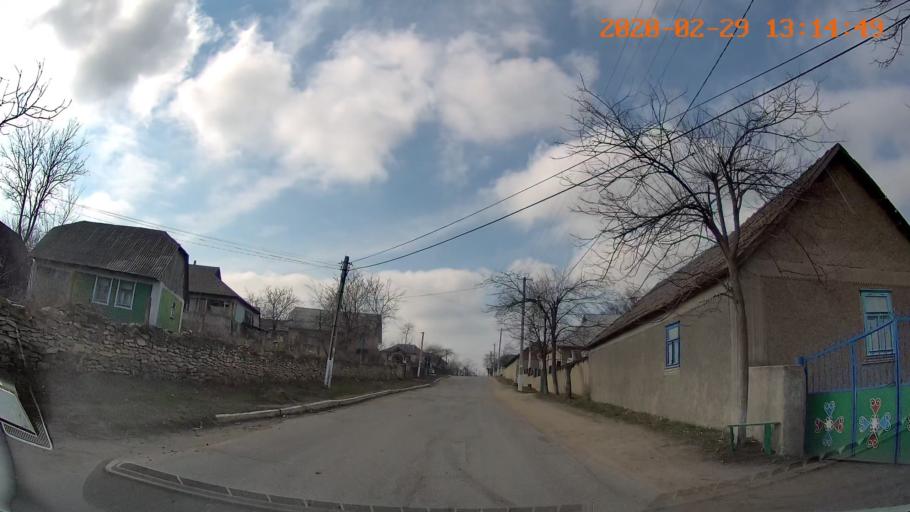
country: MD
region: Telenesti
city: Camenca
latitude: 48.0114
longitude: 28.6748
